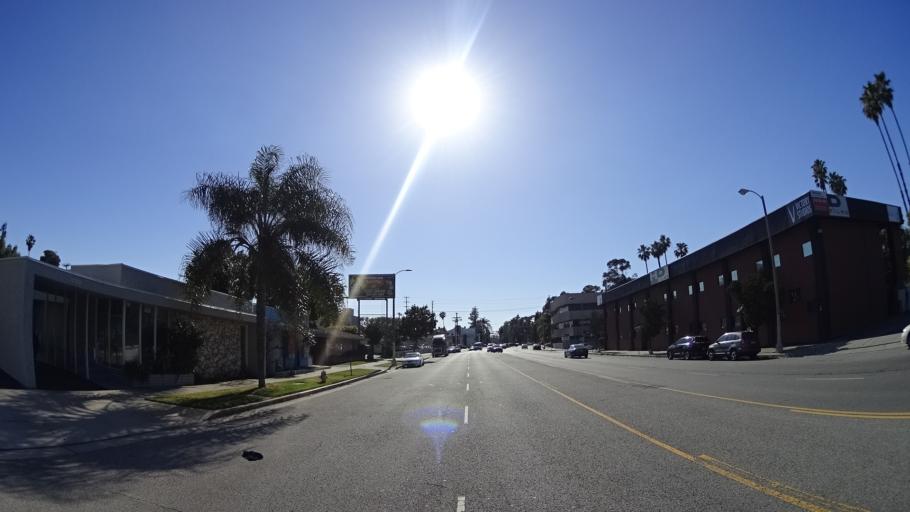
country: US
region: California
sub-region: Los Angeles County
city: Universal City
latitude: 34.1522
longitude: -118.3684
